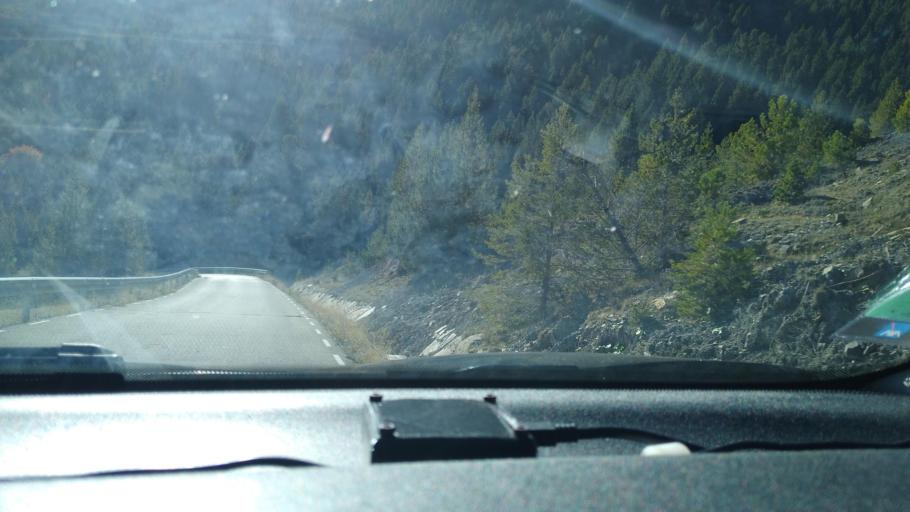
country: ES
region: Catalonia
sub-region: Provincia de Barcelona
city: Vallcebre
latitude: 42.2013
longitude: 1.7735
